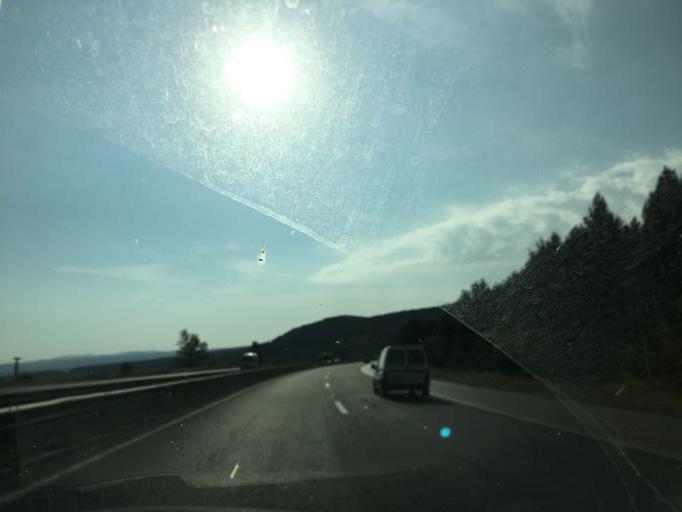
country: BG
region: Sofiya
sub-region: Obshtina Elin Pelin
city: Elin Pelin
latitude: 42.5967
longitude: 23.5874
